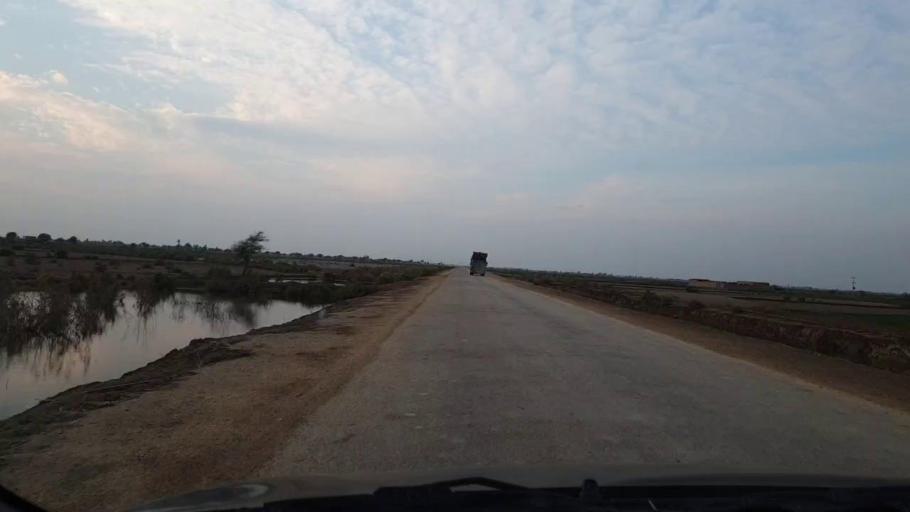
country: PK
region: Sindh
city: Sinjhoro
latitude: 25.9993
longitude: 68.8472
